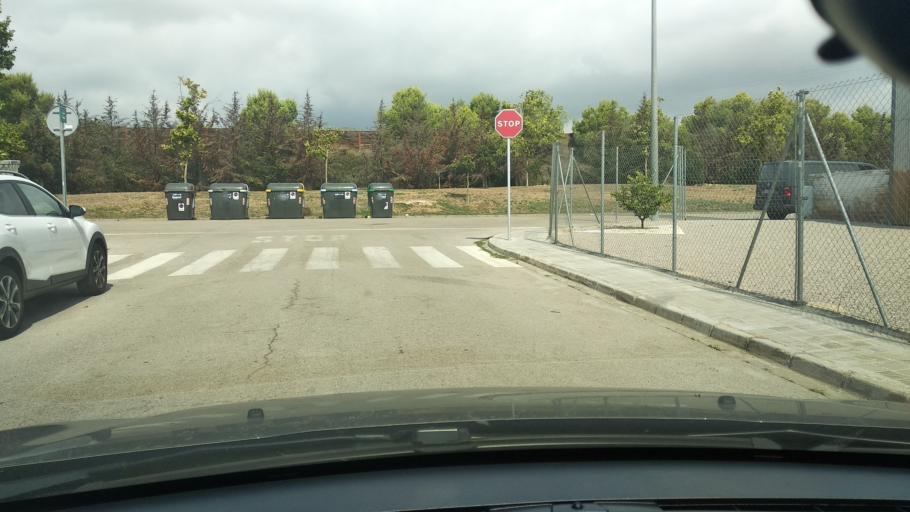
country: ES
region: Catalonia
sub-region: Provincia de Tarragona
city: El Vendrell
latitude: 41.2229
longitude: 1.5219
